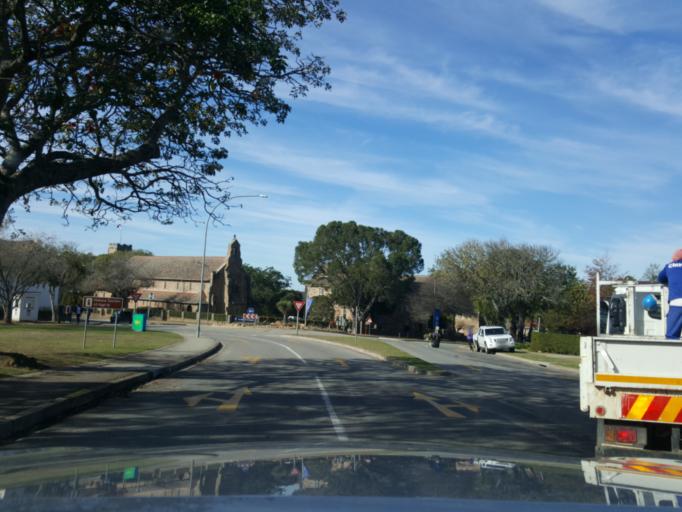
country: ZA
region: Eastern Cape
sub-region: Cacadu District Municipality
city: Grahamstown
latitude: -33.3073
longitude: 26.5173
